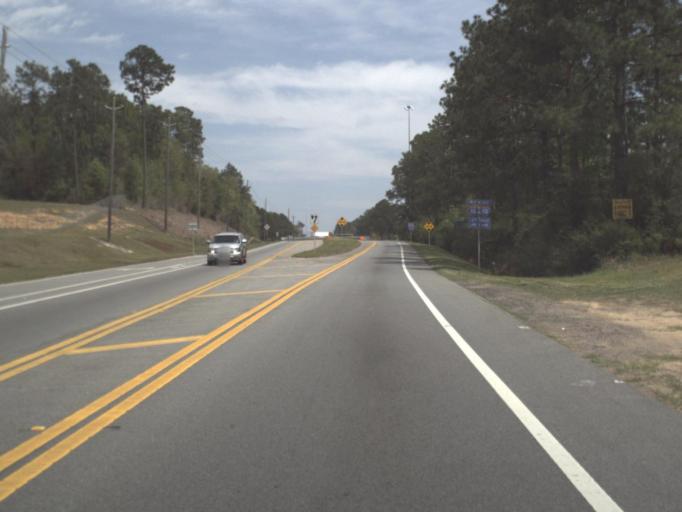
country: US
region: Florida
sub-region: Escambia County
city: Gonzalez
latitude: 30.5348
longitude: -87.3415
